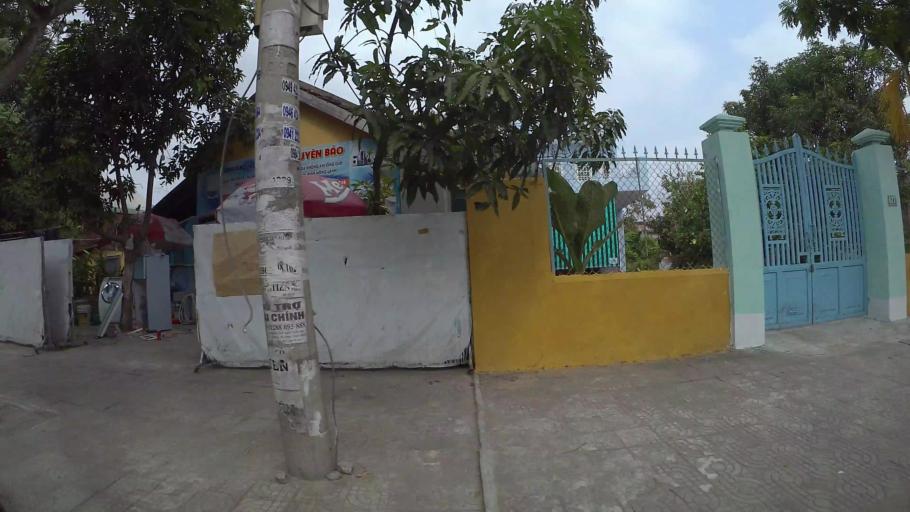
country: VN
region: Da Nang
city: Cam Le
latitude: 16.0372
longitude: 108.1842
